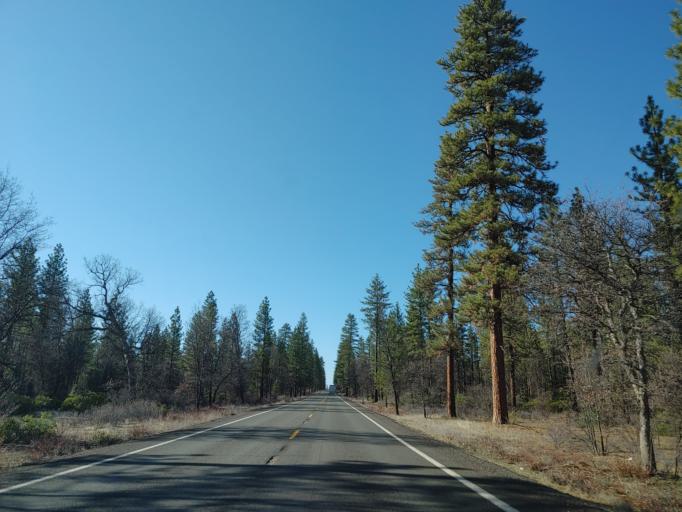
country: US
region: California
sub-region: Shasta County
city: Burney
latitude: 40.9270
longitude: -121.5998
